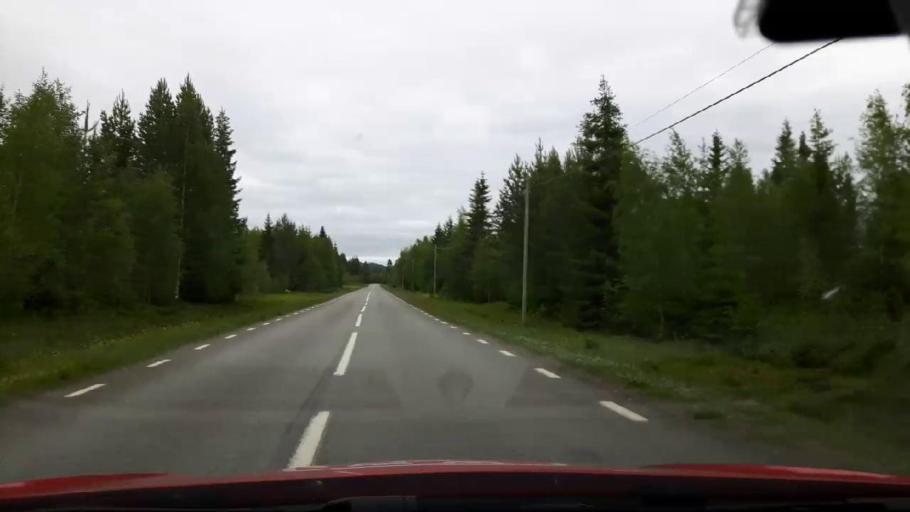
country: SE
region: Jaemtland
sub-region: Stroemsunds Kommun
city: Stroemsund
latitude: 63.3985
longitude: 15.6348
